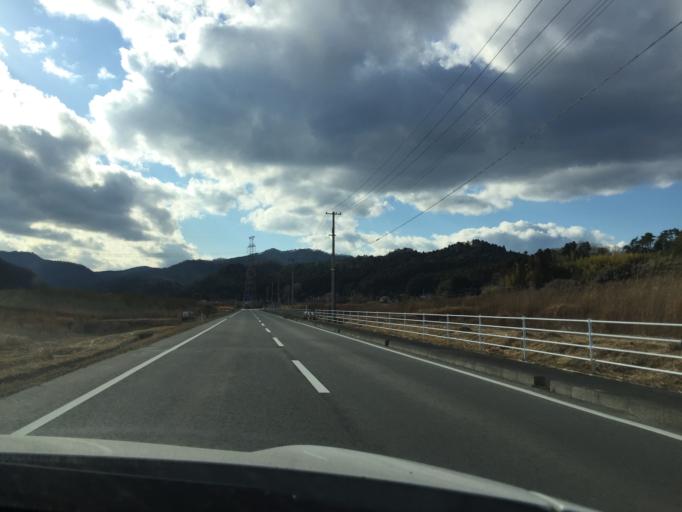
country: JP
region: Fukushima
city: Namie
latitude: 37.4135
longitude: 140.9552
